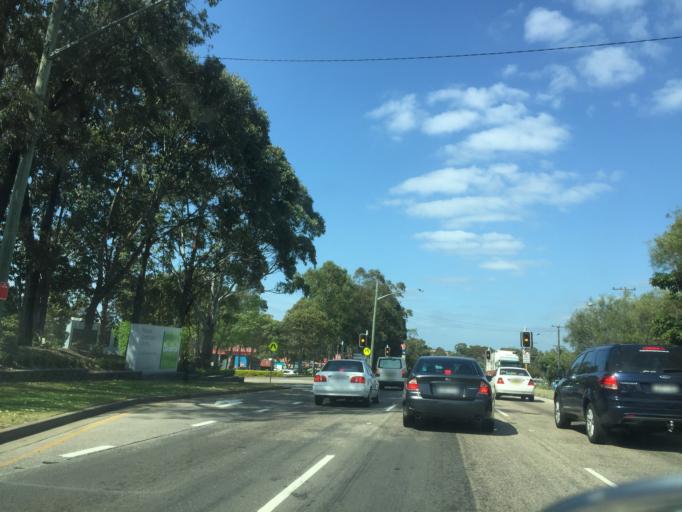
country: AU
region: New South Wales
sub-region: Canterbury
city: Belfield
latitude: -33.9030
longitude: 151.0647
